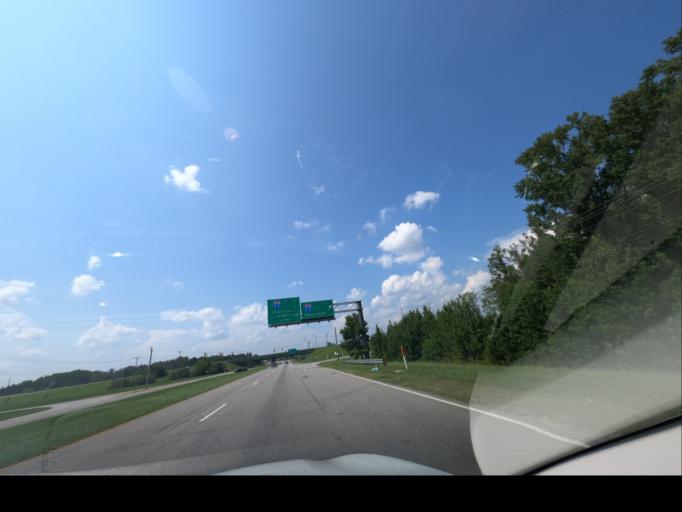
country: US
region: South Carolina
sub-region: Richland County
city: Columbia
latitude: 33.9489
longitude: -80.9892
